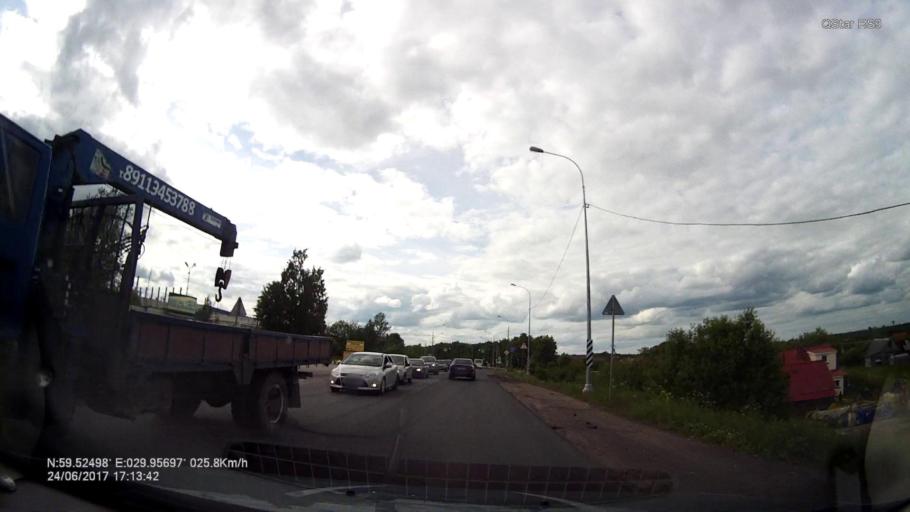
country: RU
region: Leningrad
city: Voyskovitsy
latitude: 59.5251
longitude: 29.9568
